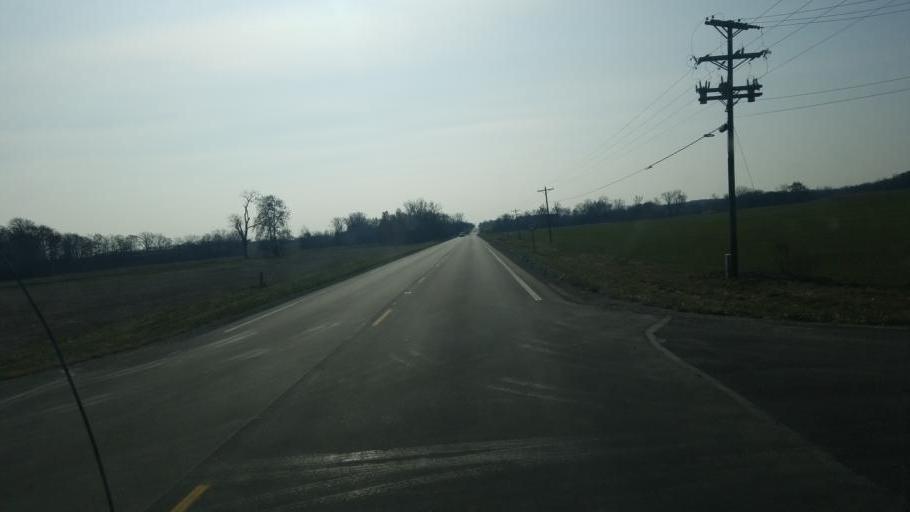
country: US
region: Ohio
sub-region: Mercer County
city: Fort Recovery
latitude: 40.4652
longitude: -84.7844
